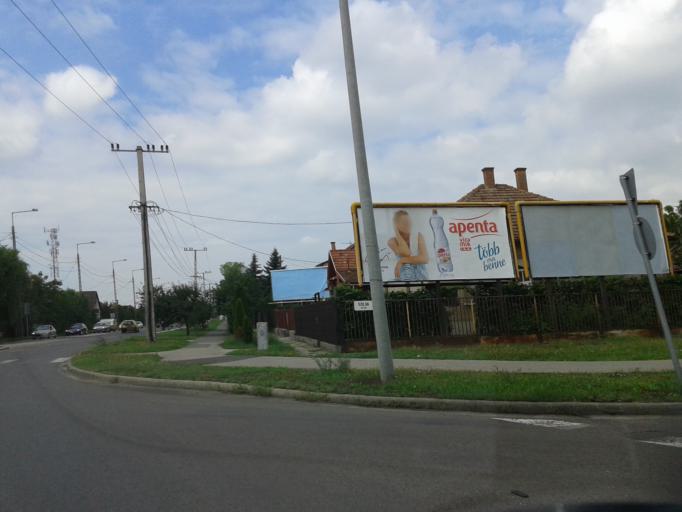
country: HU
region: Csongrad
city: Szeged
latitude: 46.2733
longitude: 20.0802
